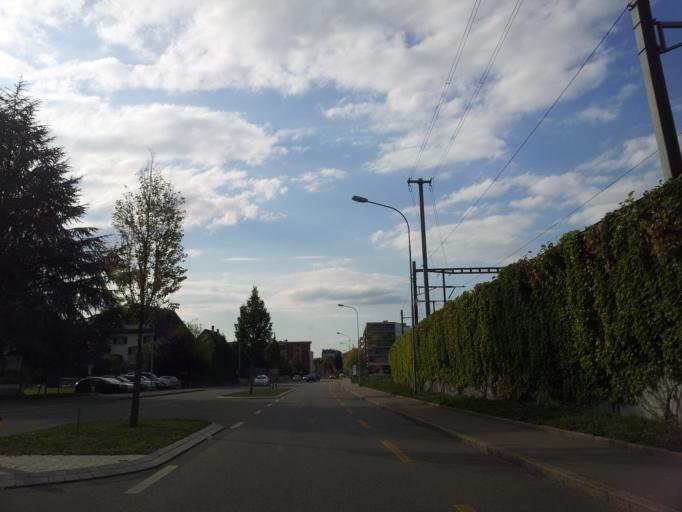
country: CH
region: Zurich
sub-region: Bezirk Dietikon
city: Dietikon / Guggenbuehl
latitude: 47.4009
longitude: 8.4093
